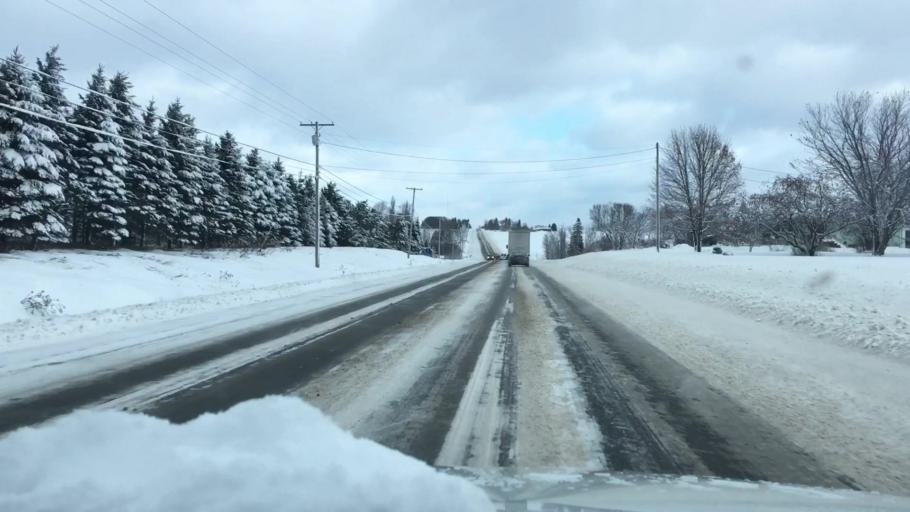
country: US
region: Maine
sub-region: Aroostook County
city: Presque Isle
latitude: 46.7443
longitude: -67.9956
